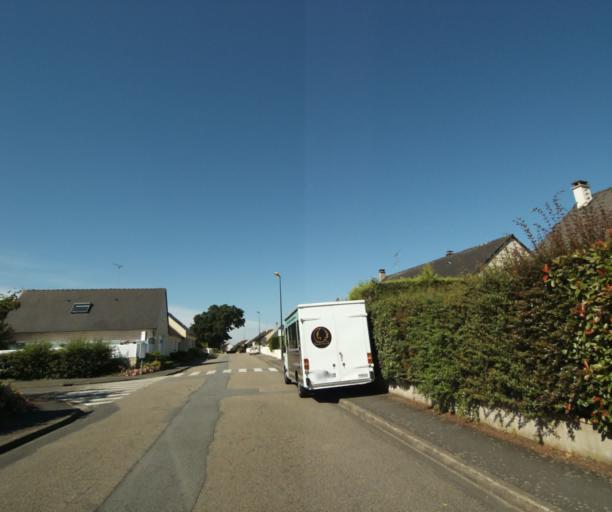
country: FR
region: Pays de la Loire
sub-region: Departement de la Mayenne
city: Laval
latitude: 48.0535
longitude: -0.7430
